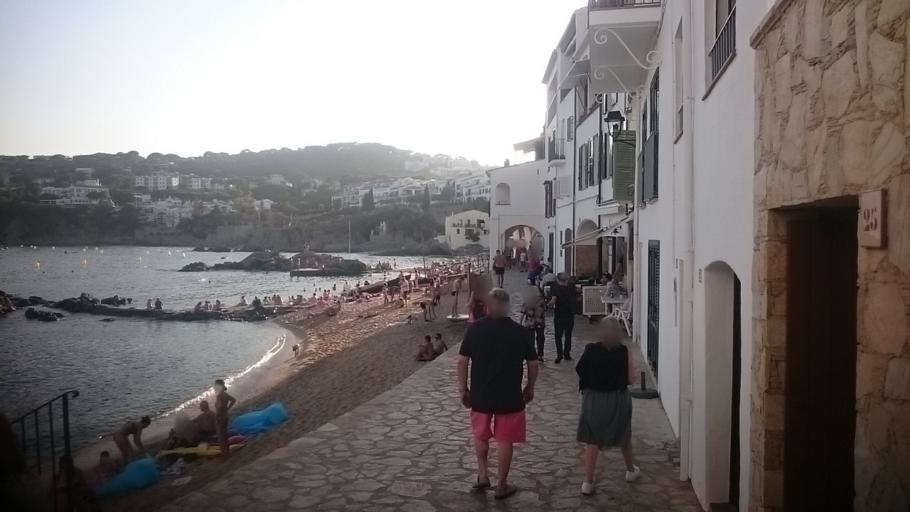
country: ES
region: Catalonia
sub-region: Provincia de Girona
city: Palafrugell
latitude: 41.8884
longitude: 3.1861
